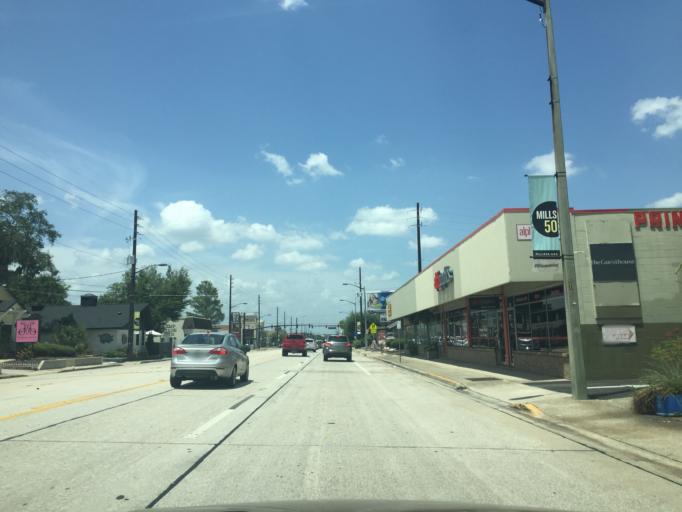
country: US
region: Florida
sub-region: Orange County
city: Orlando
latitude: 28.5626
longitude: -81.3644
